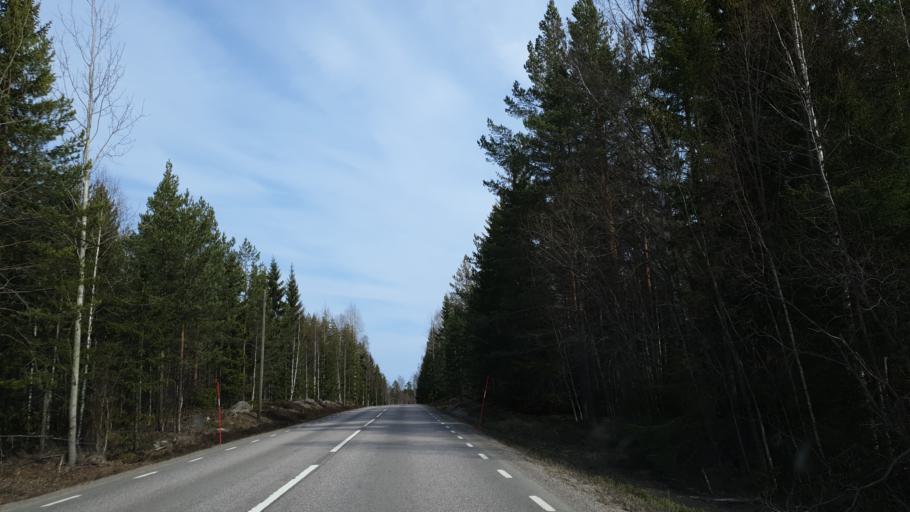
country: SE
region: Gaevleborg
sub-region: Gavle Kommun
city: Norrsundet
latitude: 60.9823
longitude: 17.0683
